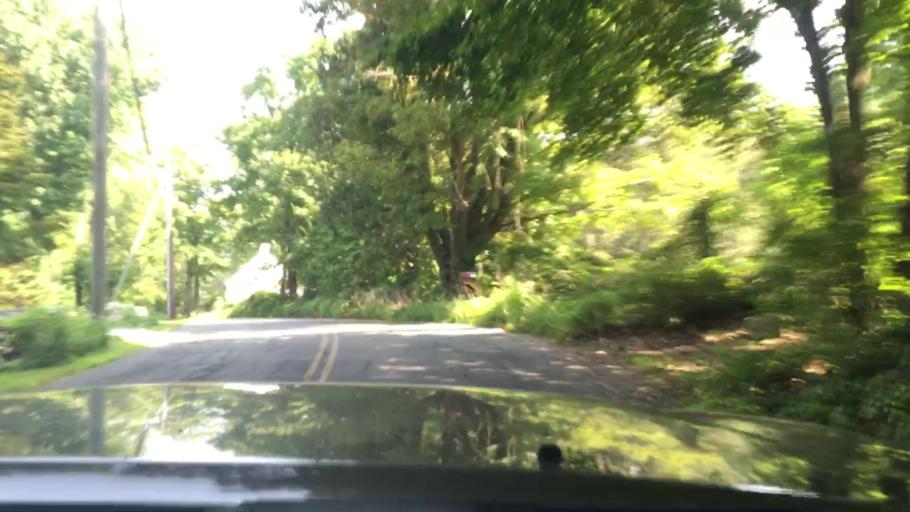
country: US
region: Connecticut
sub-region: Fairfield County
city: Georgetown
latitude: 41.2422
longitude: -73.4567
